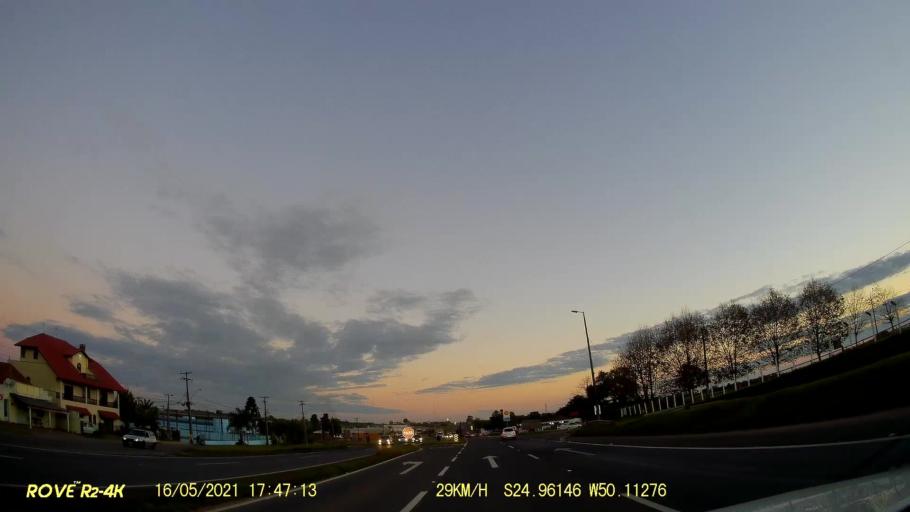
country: BR
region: Parana
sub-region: Carambei
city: Carambei
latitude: -24.9614
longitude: -50.1127
